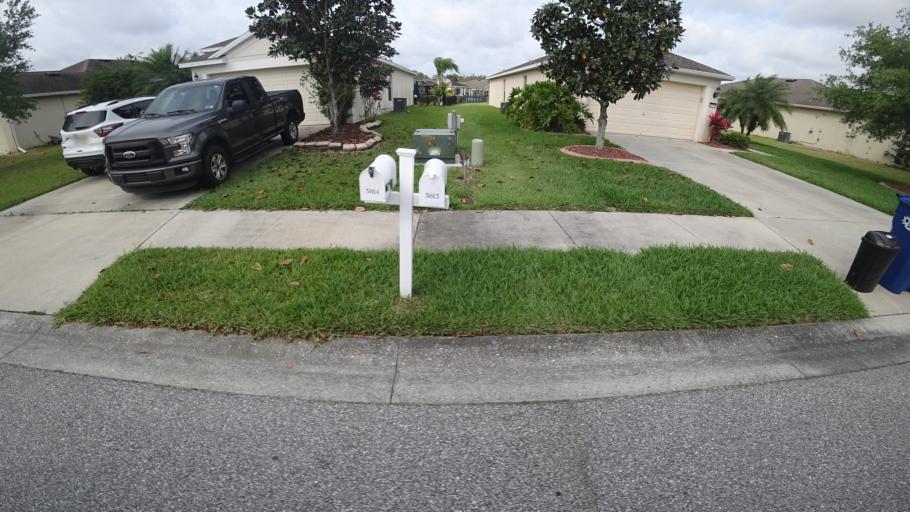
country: US
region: Florida
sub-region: Manatee County
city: Ellenton
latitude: 27.5582
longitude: -82.4642
